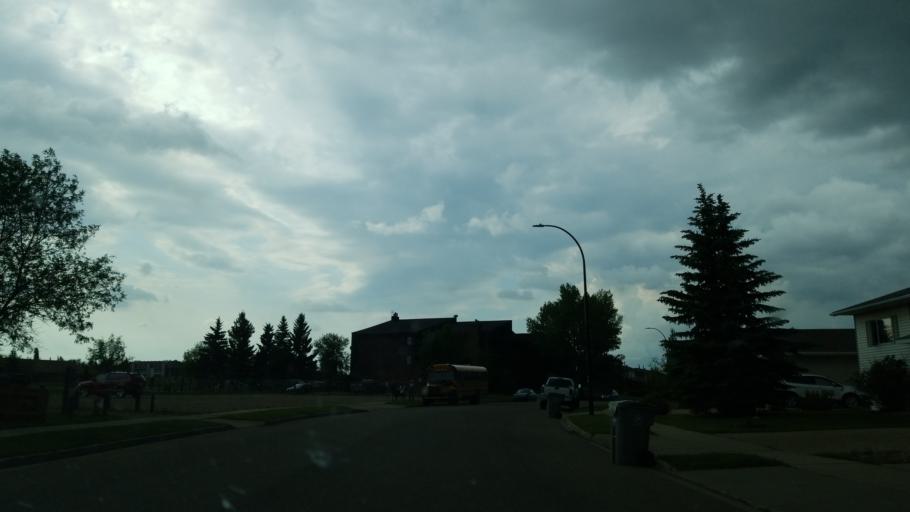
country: CA
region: Saskatchewan
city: Lloydminster
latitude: 53.2642
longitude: -110.0210
